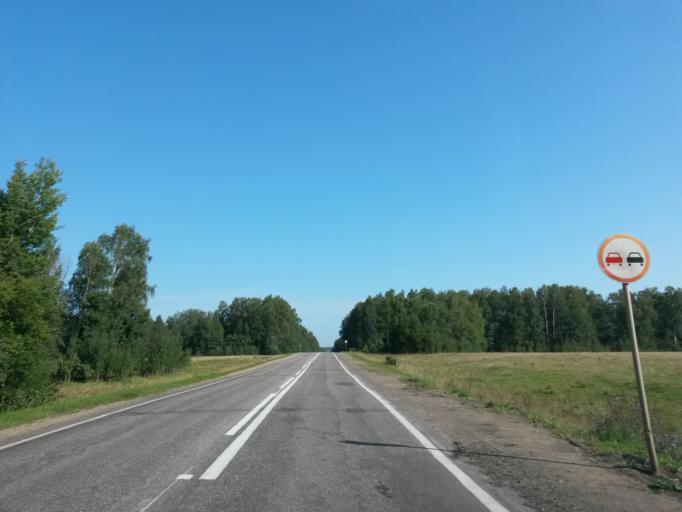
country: RU
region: Jaroslavl
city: Gavrilov-Yam
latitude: 57.4136
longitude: 39.9204
